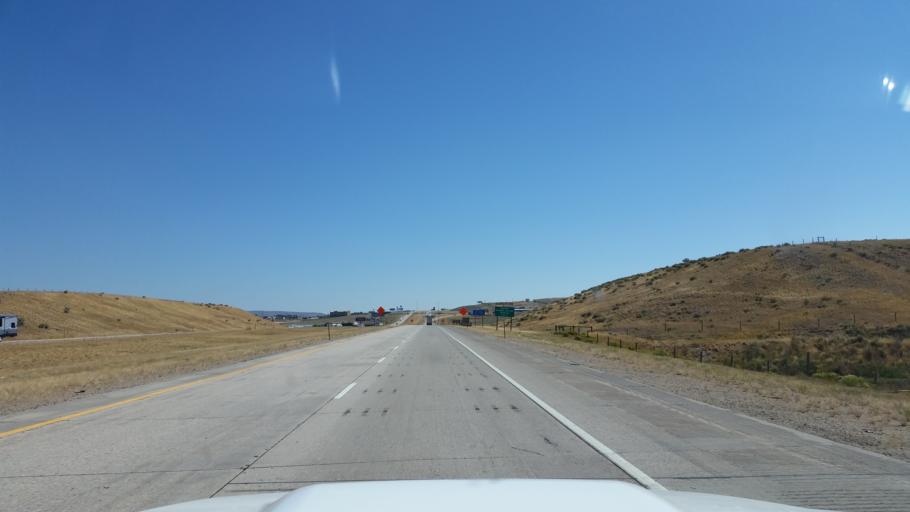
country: US
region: Wyoming
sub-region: Uinta County
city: Evanston
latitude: 41.2514
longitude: -111.0055
